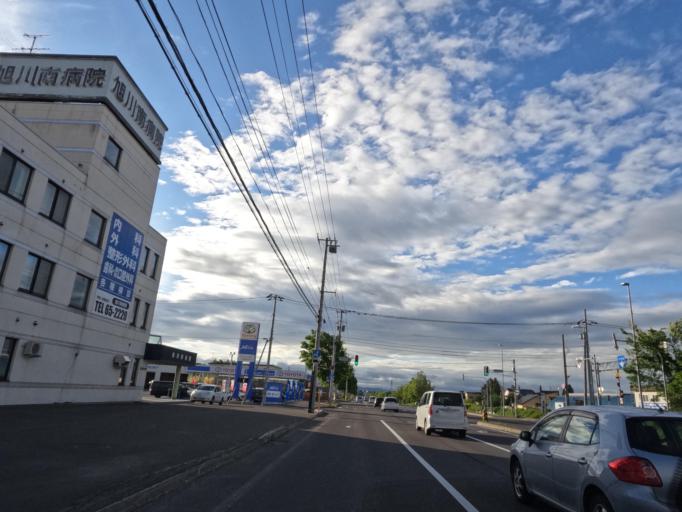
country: JP
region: Hokkaido
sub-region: Asahikawa-shi
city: Asahikawa
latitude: 43.7348
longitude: 142.3630
